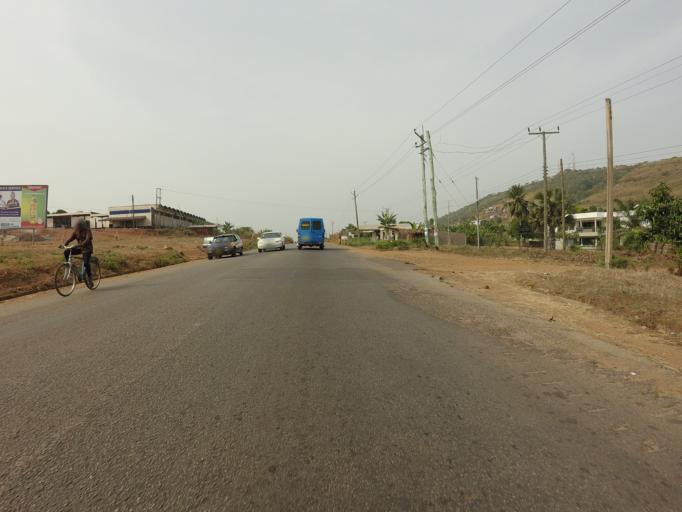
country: GH
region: Volta
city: Ho
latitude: 6.6081
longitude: 0.4555
